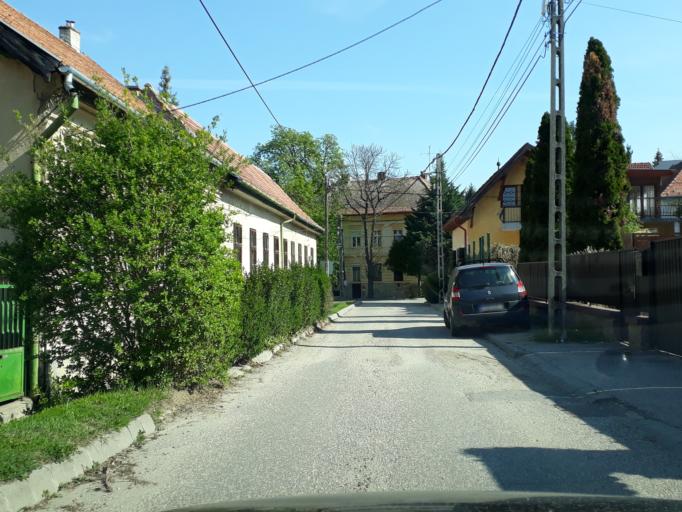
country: HU
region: Pest
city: Budakeszi
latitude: 47.5107
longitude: 18.9360
